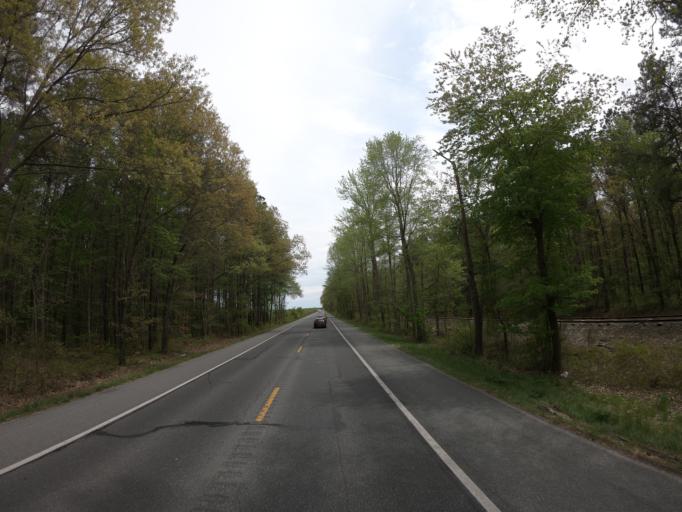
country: US
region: Delaware
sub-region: Sussex County
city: Milton
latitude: 38.7898
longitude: -75.3705
